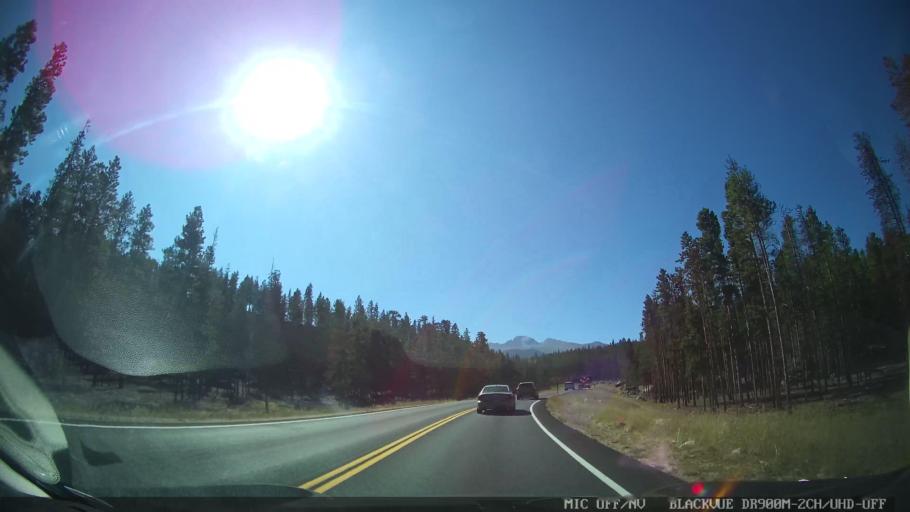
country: US
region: Colorado
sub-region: Larimer County
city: Estes Park
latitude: 40.3383
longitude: -105.6005
